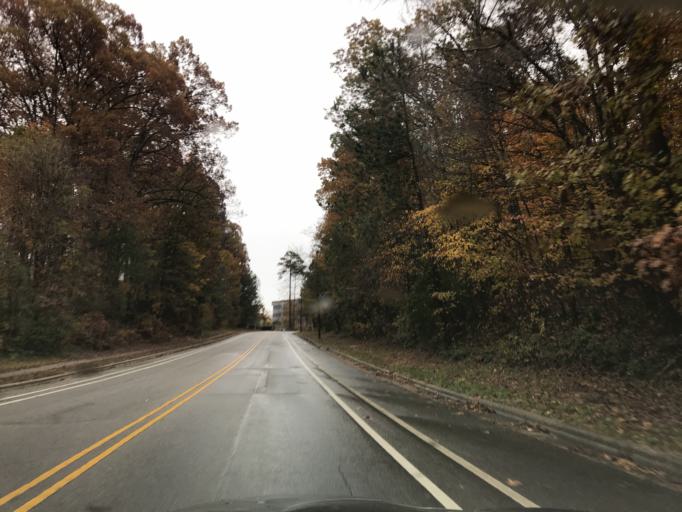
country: US
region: North Carolina
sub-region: Wake County
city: West Raleigh
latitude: 35.8339
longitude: -78.6256
